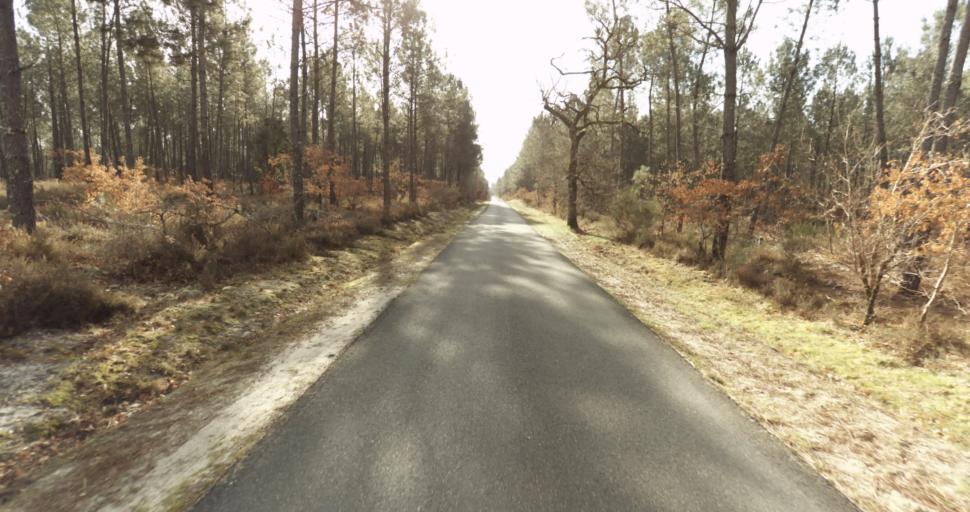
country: FR
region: Aquitaine
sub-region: Departement des Landes
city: Roquefort
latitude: 44.0739
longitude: -0.2680
